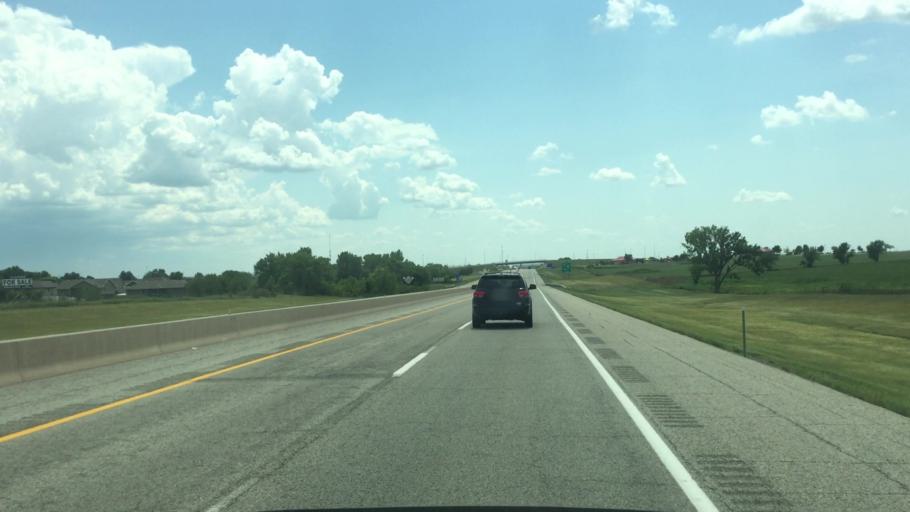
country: US
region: Kansas
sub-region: Lyon County
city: Emporia
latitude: 38.4270
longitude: -96.2292
